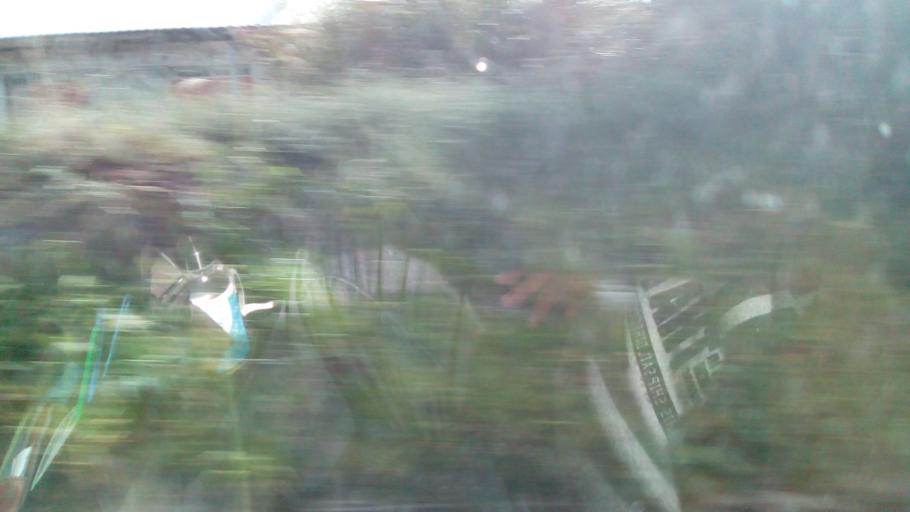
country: TW
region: Taiwan
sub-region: Hualien
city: Hualian
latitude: 24.3613
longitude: 121.3314
